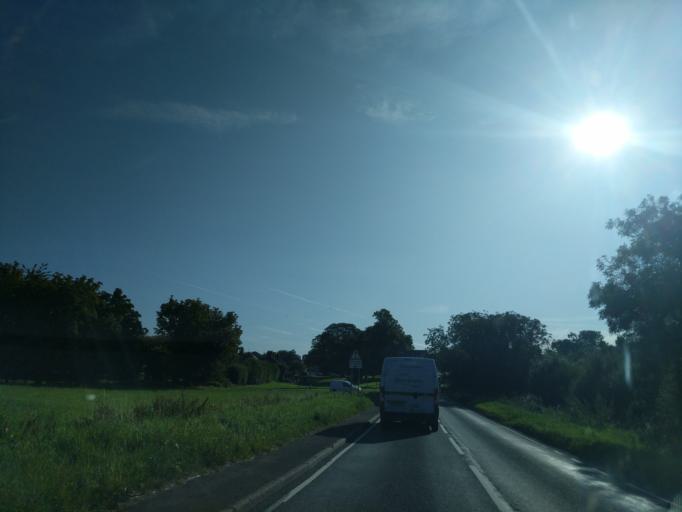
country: GB
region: England
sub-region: District of Rutland
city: Clipsham
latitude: 52.8122
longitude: -0.5246
